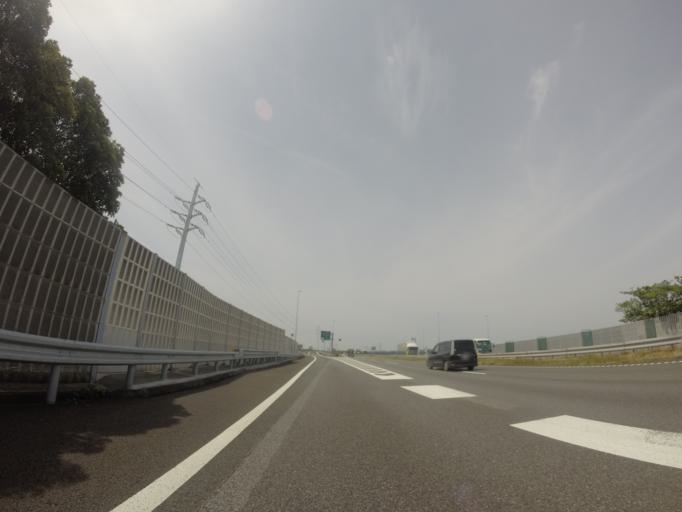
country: JP
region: Shizuoka
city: Fujieda
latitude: 34.8201
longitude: 138.2681
